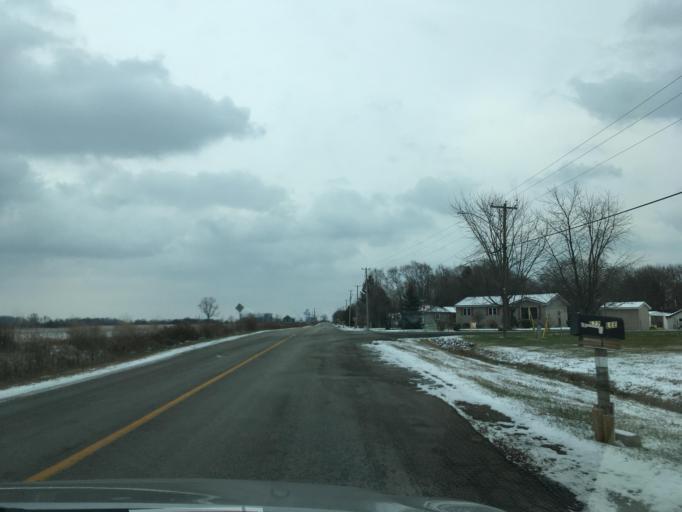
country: CA
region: Ontario
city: Norfolk County
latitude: 42.7882
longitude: -80.1382
